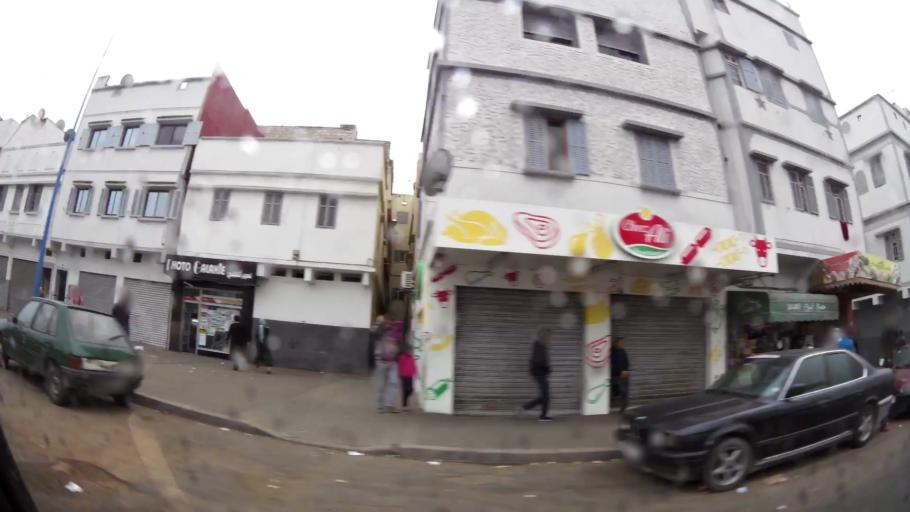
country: MA
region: Grand Casablanca
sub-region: Casablanca
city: Casablanca
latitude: 33.5633
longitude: -7.5627
